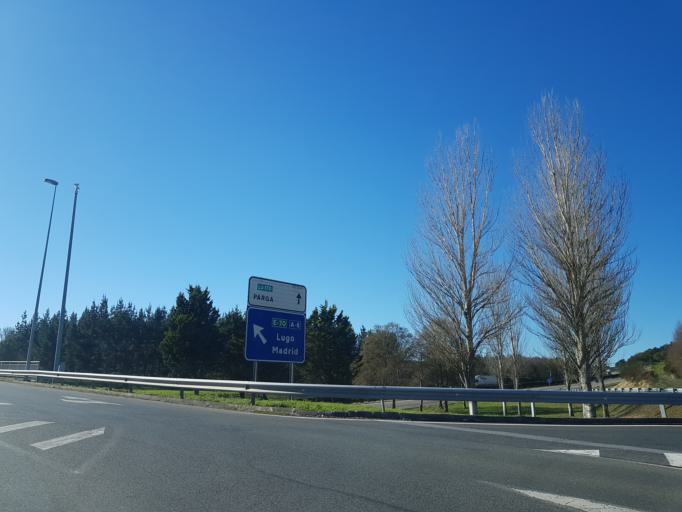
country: ES
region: Galicia
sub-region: Provincia de Lugo
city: Guitiriz
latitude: 43.1847
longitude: -7.8246
